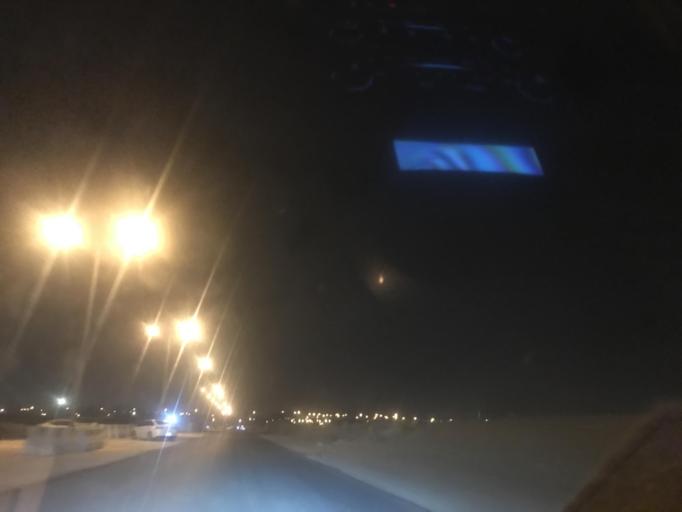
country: SA
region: Ar Riyad
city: Riyadh
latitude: 24.7622
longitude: 46.5886
